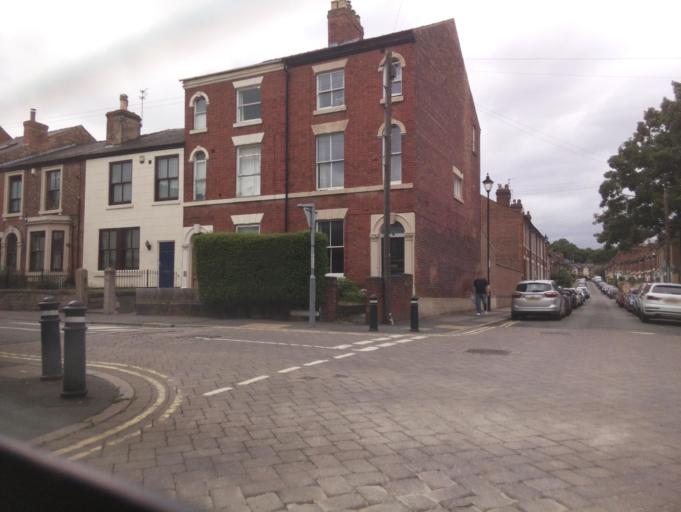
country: GB
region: England
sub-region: Derby
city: Derby
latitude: 52.9295
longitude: -1.4802
